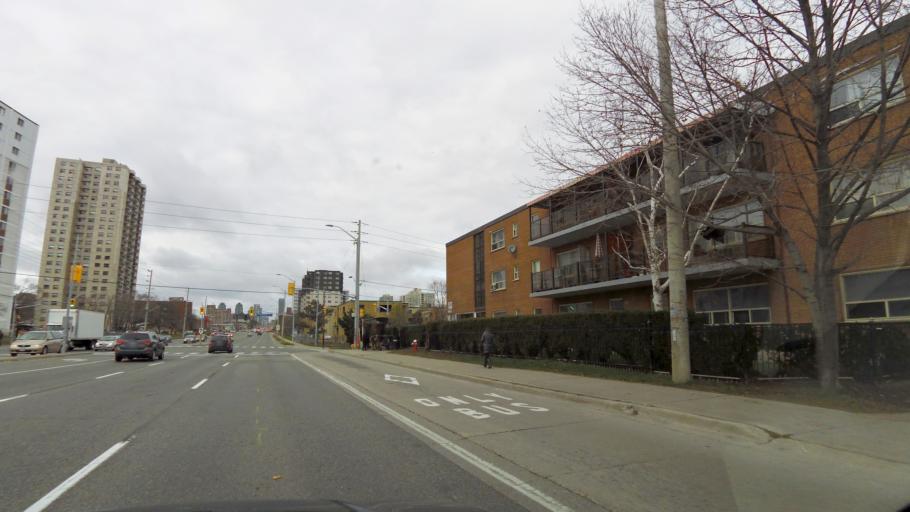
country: CA
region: Ontario
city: Mississauga
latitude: 43.5756
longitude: -79.6095
